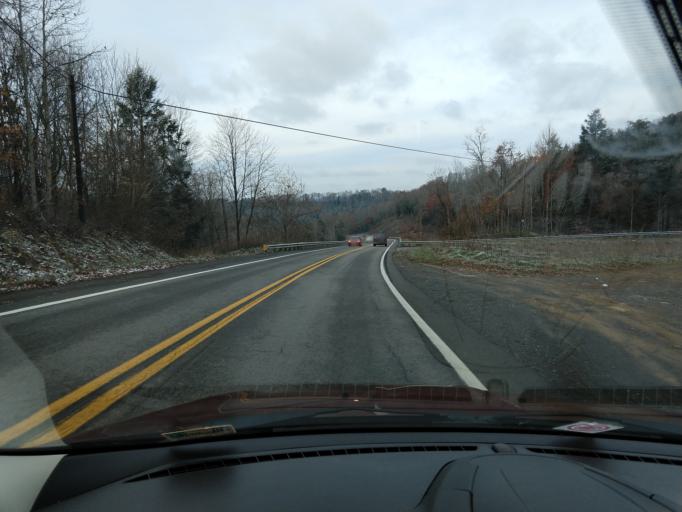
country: US
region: West Virginia
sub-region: Nicholas County
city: Craigsville
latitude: 38.2473
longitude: -80.7202
